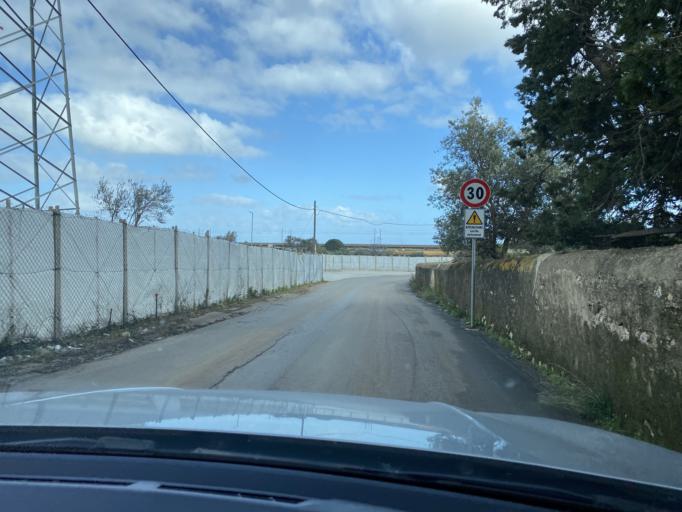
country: IT
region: Sicily
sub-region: Palermo
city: Carini
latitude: 38.1489
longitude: 13.1650
